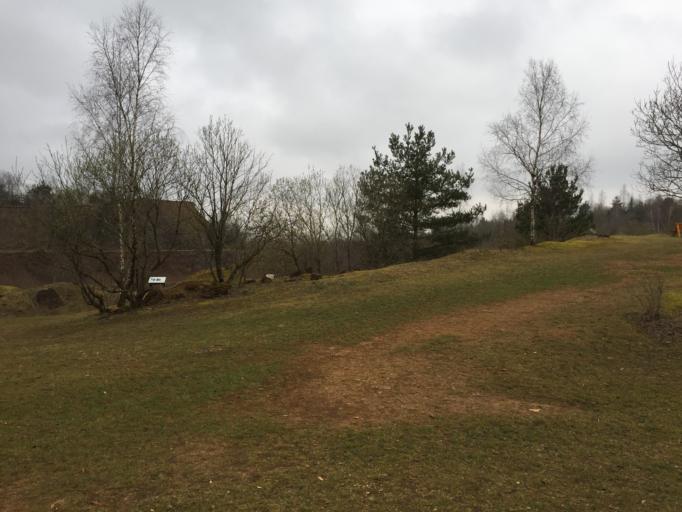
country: LU
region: Luxembourg
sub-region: Canton d'Esch-sur-Alzette
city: Niedercorn
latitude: 49.5415
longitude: 5.8828
